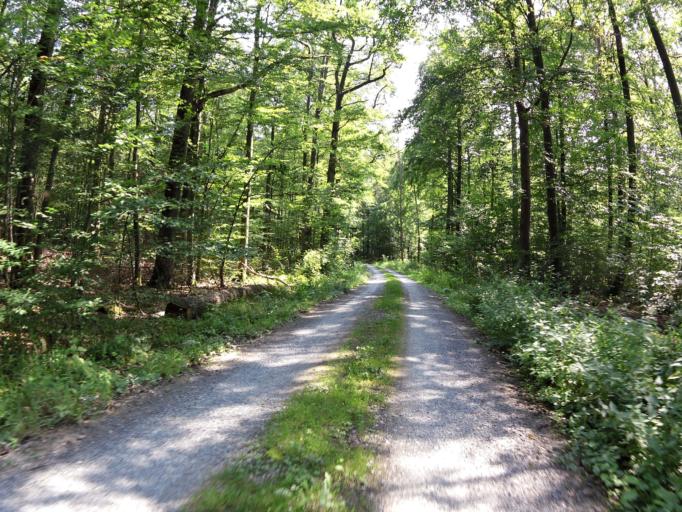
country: DE
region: Bavaria
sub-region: Regierungsbezirk Unterfranken
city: Kleinrinderfeld
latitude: 49.7150
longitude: 9.8063
